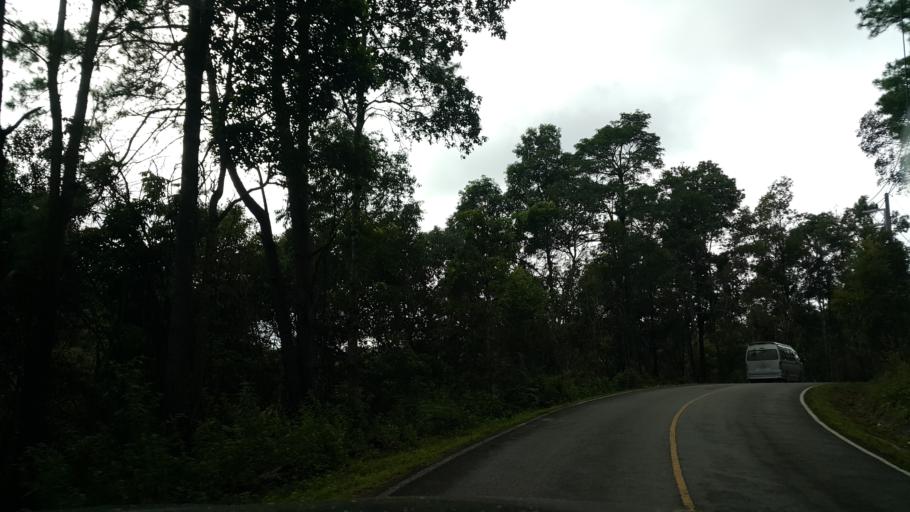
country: TH
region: Chiang Mai
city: Chaem Luang
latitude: 18.9151
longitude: 98.4922
